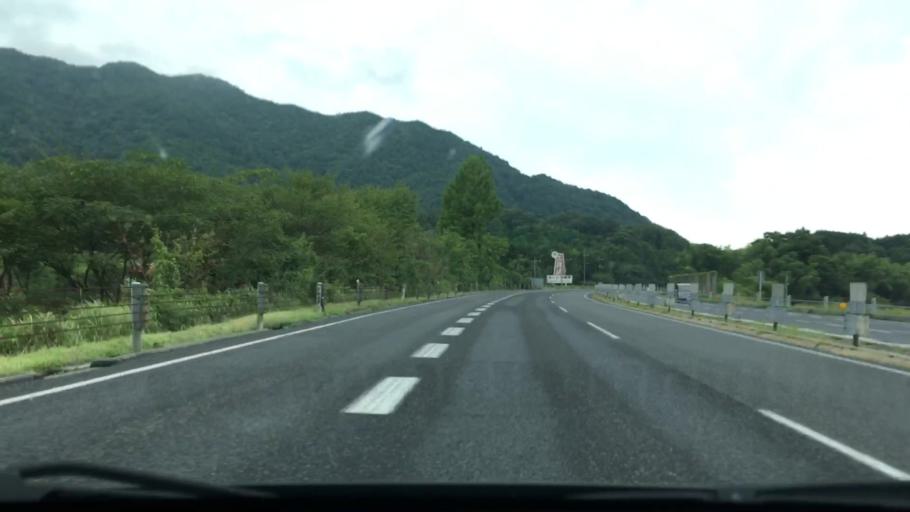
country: JP
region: Hiroshima
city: Hiroshima-shi
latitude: 34.6348
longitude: 132.5141
